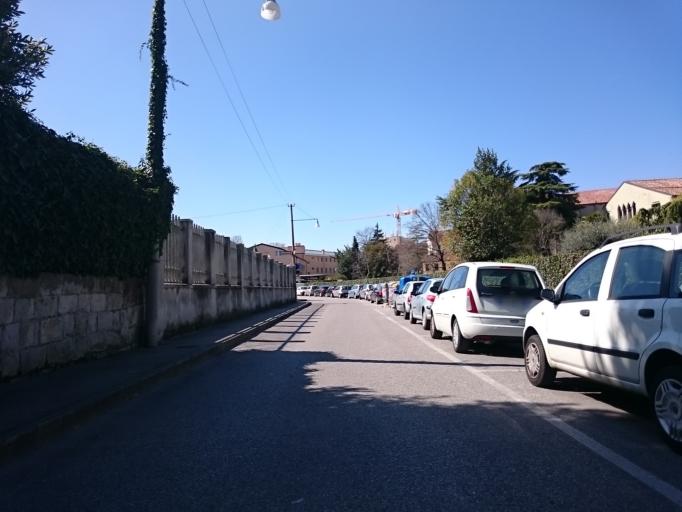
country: IT
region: Veneto
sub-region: Provincia di Padova
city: Padova
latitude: 45.4009
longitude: 11.8826
